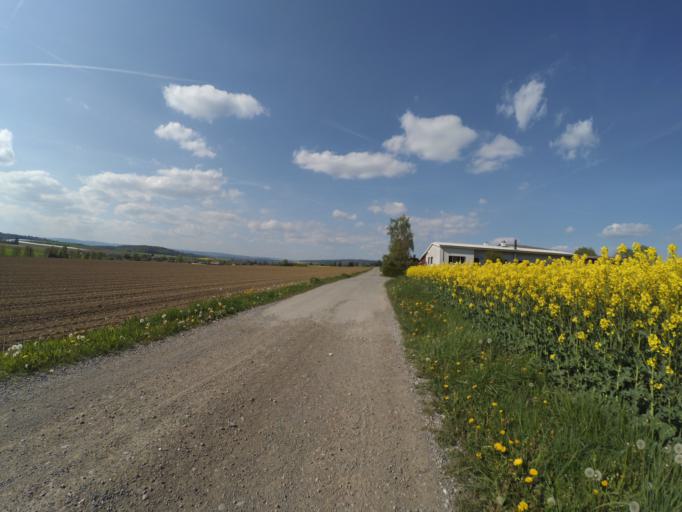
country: CH
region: Thurgau
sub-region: Frauenfeld District
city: Diessenhofen
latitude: 47.6604
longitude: 8.7521
